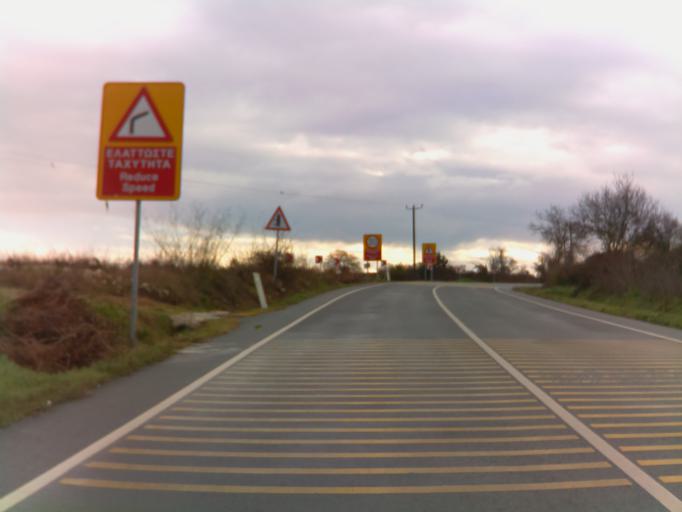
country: CY
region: Pafos
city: Pegeia
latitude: 34.9109
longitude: 32.4345
